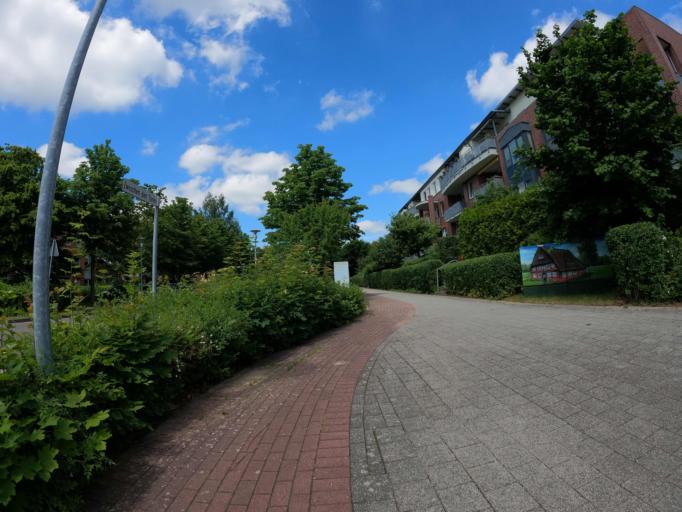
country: DE
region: Schleswig-Holstein
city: Wentorf bei Hamburg
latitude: 53.4892
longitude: 10.2571
